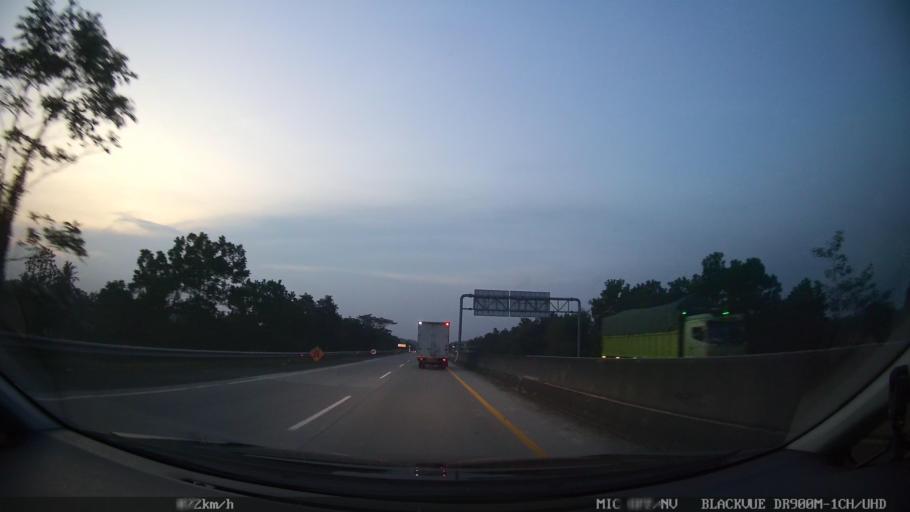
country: ID
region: Lampung
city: Sidorejo
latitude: -5.5676
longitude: 105.5362
